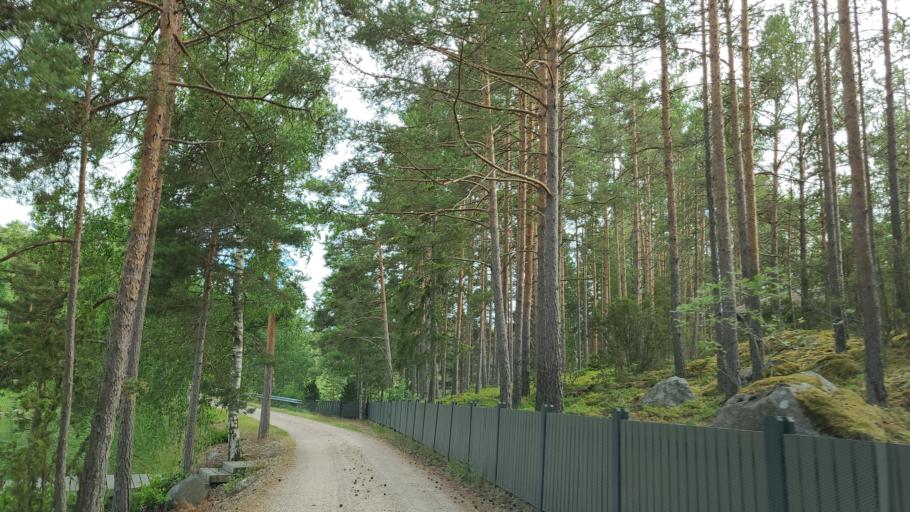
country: FI
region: Varsinais-Suomi
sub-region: Aboland-Turunmaa
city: Nagu
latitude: 60.1308
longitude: 21.7980
